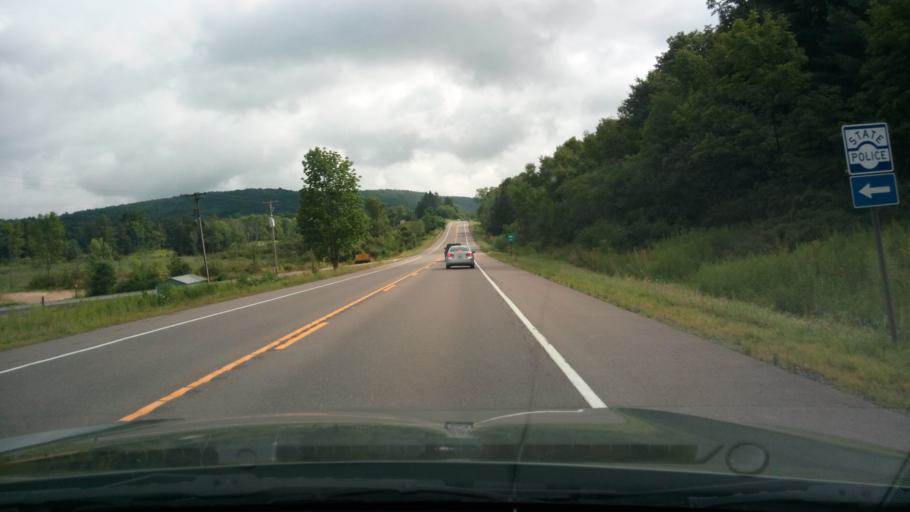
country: US
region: New York
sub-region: Tompkins County
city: Northwest Ithaca
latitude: 42.3449
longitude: -76.6211
